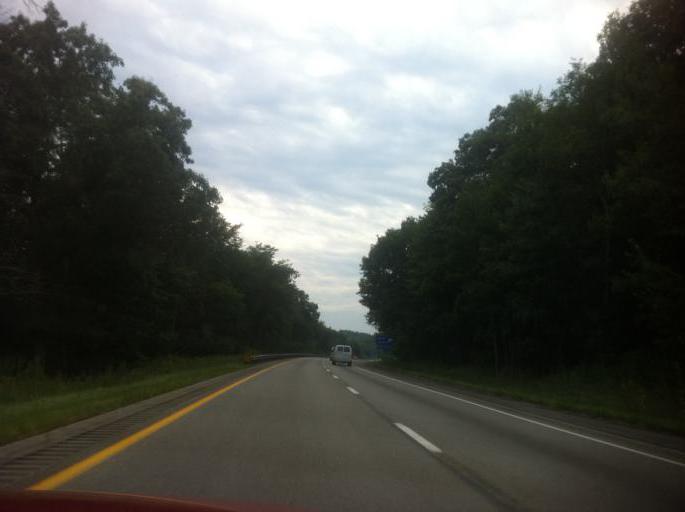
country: US
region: Pennsylvania
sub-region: Mercer County
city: Grove City
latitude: 41.2022
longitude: -79.9390
